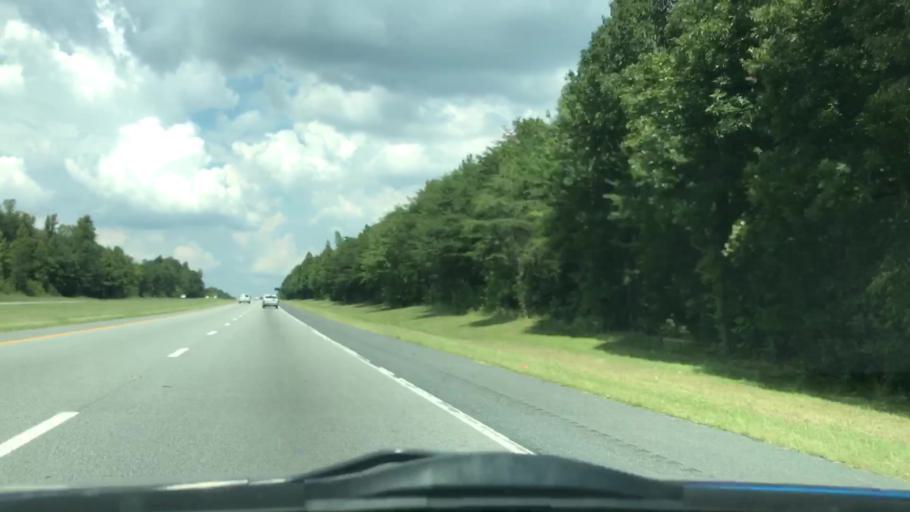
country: US
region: North Carolina
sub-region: Guilford County
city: Pleasant Garden
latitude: 35.9595
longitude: -79.8196
